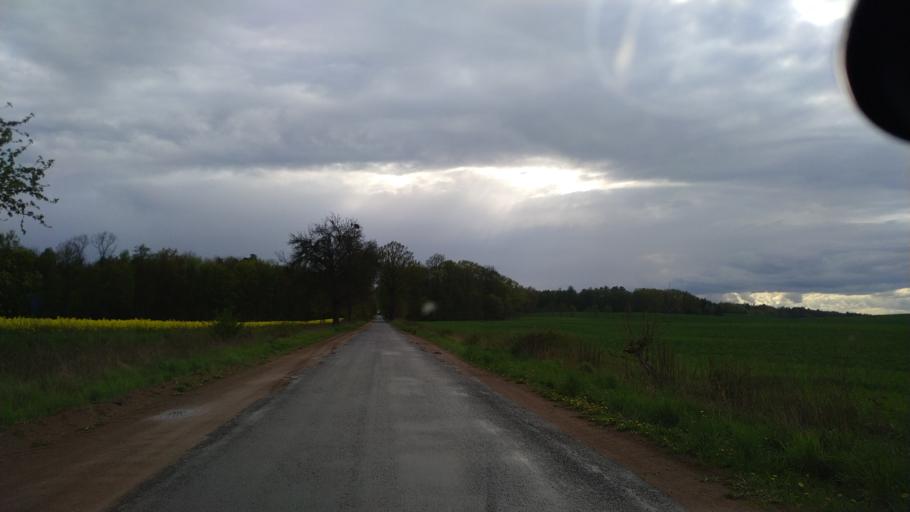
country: PL
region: Pomeranian Voivodeship
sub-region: Powiat starogardzki
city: Smetowo Graniczne
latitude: 53.7127
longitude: 18.5952
